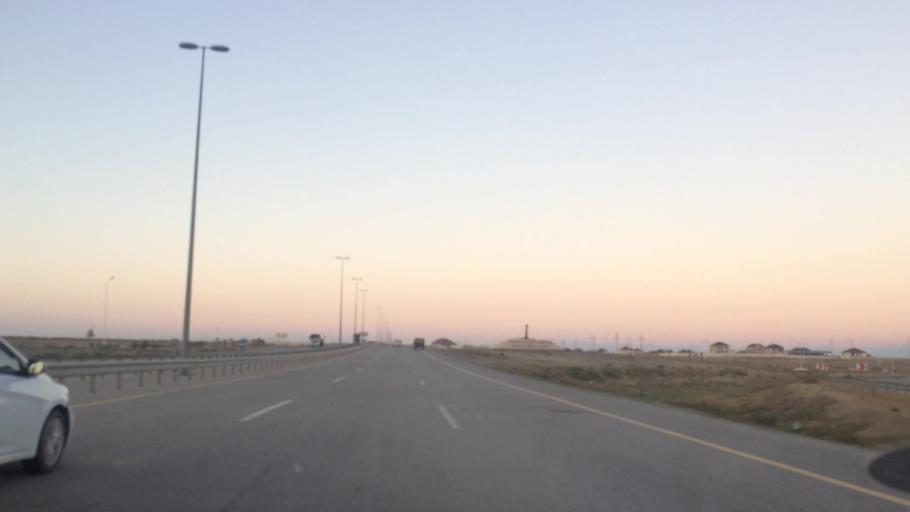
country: AZ
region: Baki
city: Qobustan
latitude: 39.9797
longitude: 49.4221
